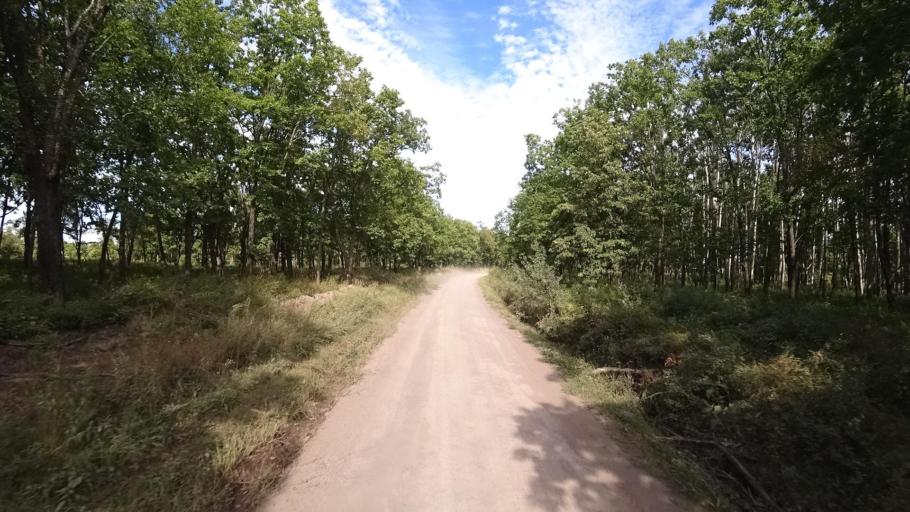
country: RU
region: Primorskiy
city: Yakovlevka
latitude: 44.3946
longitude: 133.5539
